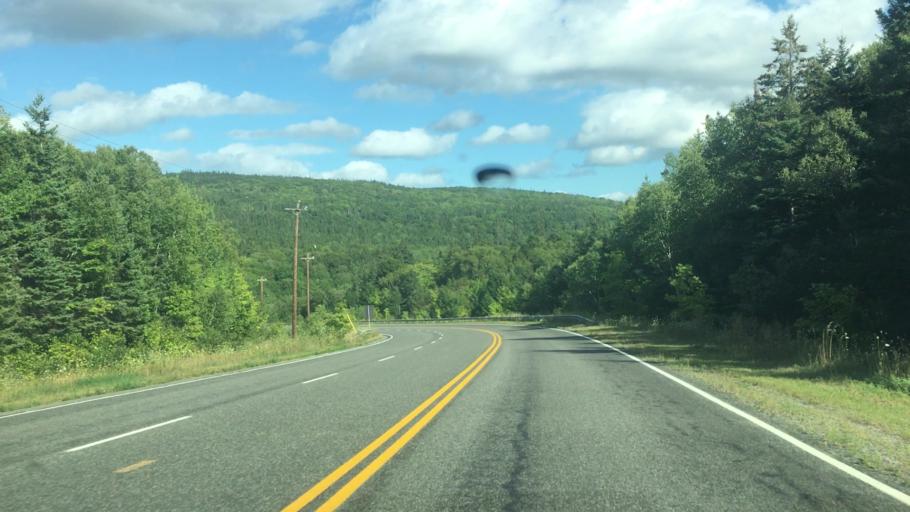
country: CA
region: Nova Scotia
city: Sydney
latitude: 45.8134
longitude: -60.6761
